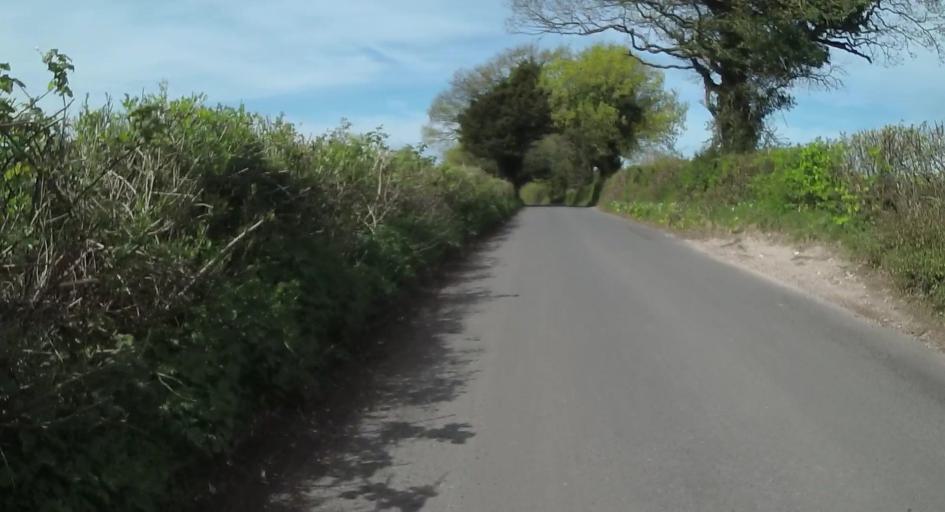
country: GB
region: England
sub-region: Hampshire
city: Compton
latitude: 51.0598
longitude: -1.3663
